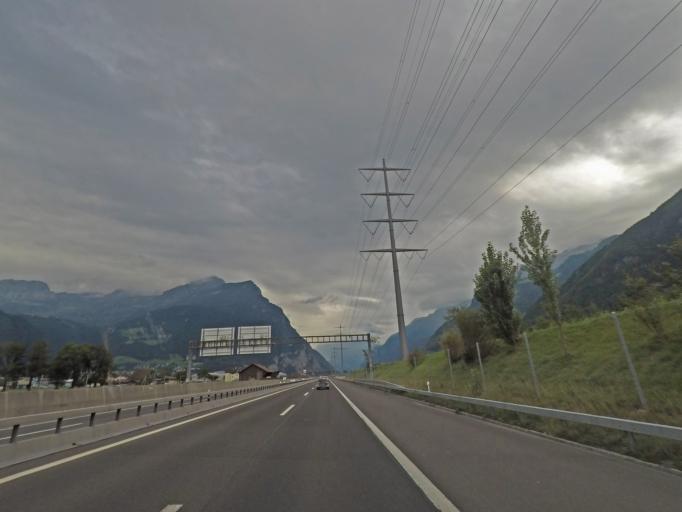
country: CH
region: Uri
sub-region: Uri
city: Seedorf
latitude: 46.8782
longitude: 8.6247
